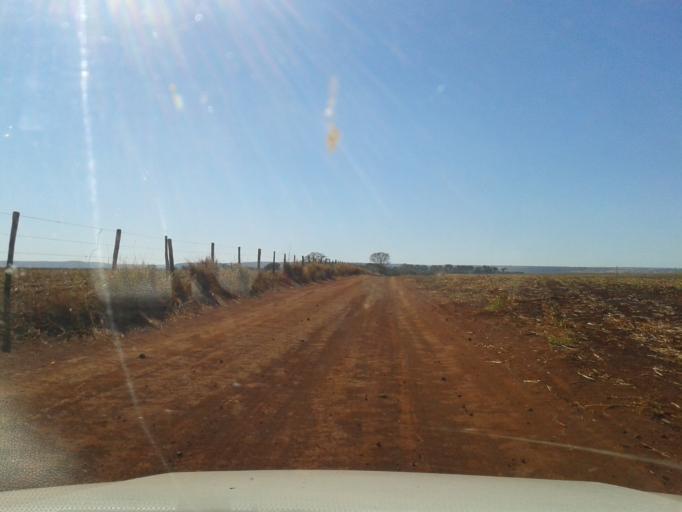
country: BR
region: Minas Gerais
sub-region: Centralina
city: Centralina
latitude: -18.5905
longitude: -49.1629
